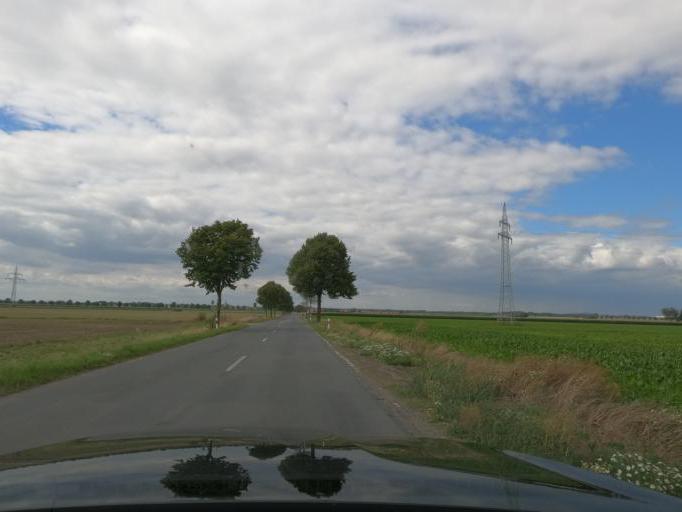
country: DE
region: Lower Saxony
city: Algermissen
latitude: 52.2450
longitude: 10.0004
